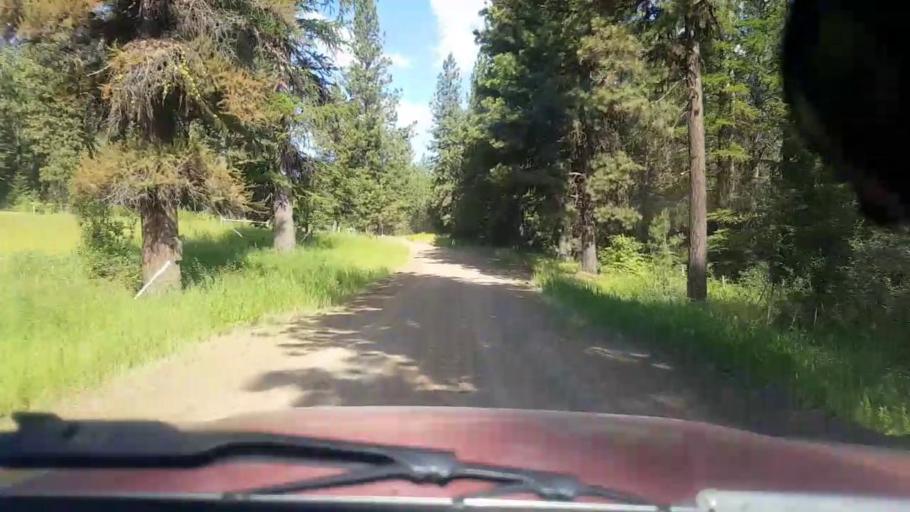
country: US
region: Washington
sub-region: Asotin County
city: Asotin
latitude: 46.0369
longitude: -117.4120
